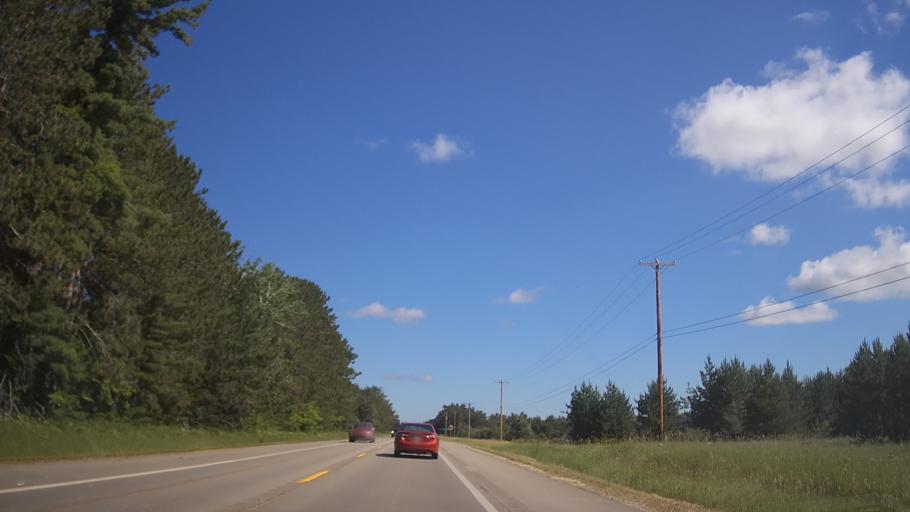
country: US
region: Michigan
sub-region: Cheboygan County
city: Indian River
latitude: 45.4823
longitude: -84.7811
